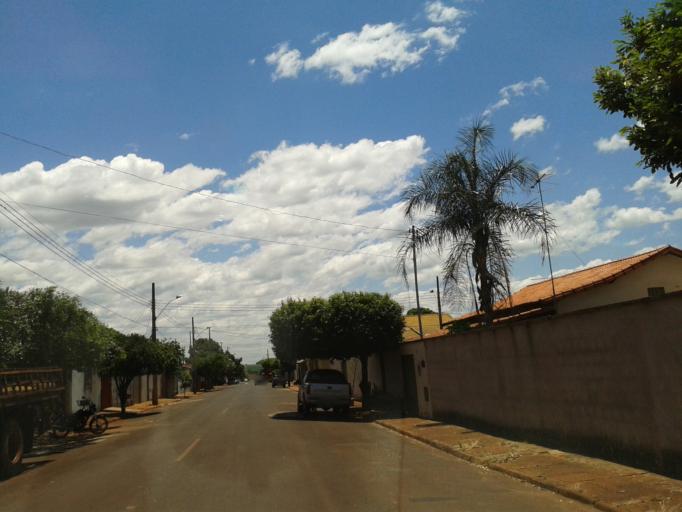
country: BR
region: Minas Gerais
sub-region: Centralina
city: Centralina
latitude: -18.7227
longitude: -49.1988
